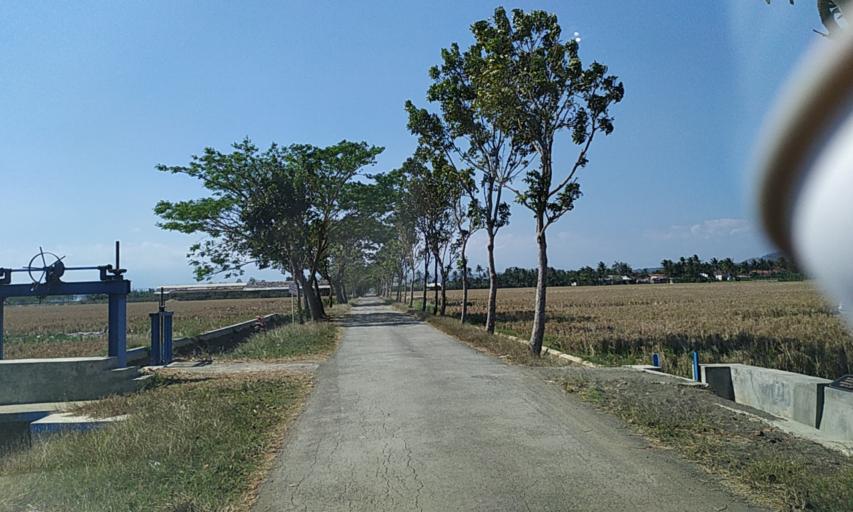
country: ID
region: Central Java
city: Mernek
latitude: -7.6001
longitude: 109.1712
